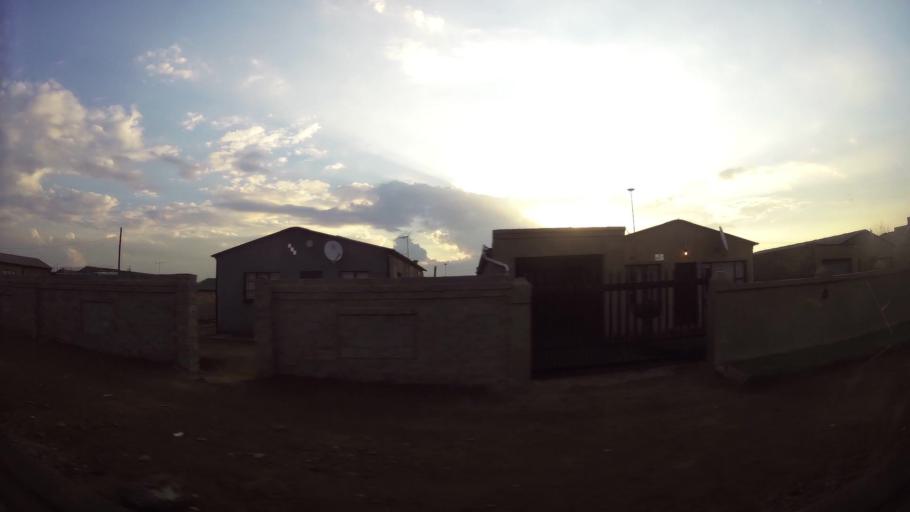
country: ZA
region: Gauteng
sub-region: City of Johannesburg Metropolitan Municipality
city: Orange Farm
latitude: -26.5520
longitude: 27.8638
